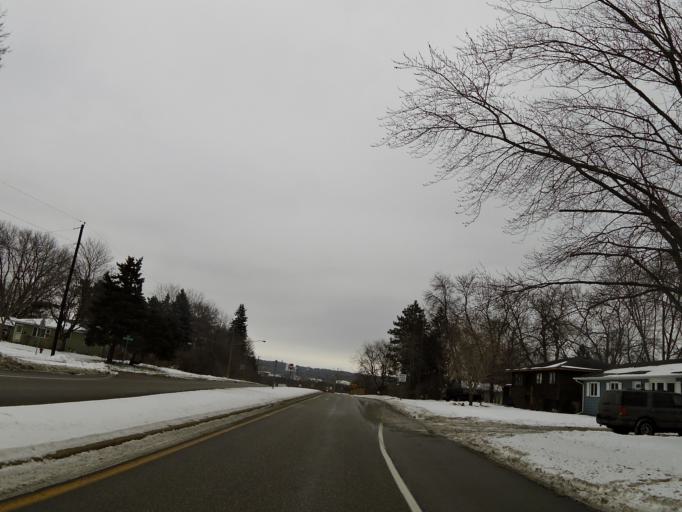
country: US
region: Minnesota
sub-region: Dakota County
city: Inver Grove Heights
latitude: 44.8480
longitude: -93.0233
